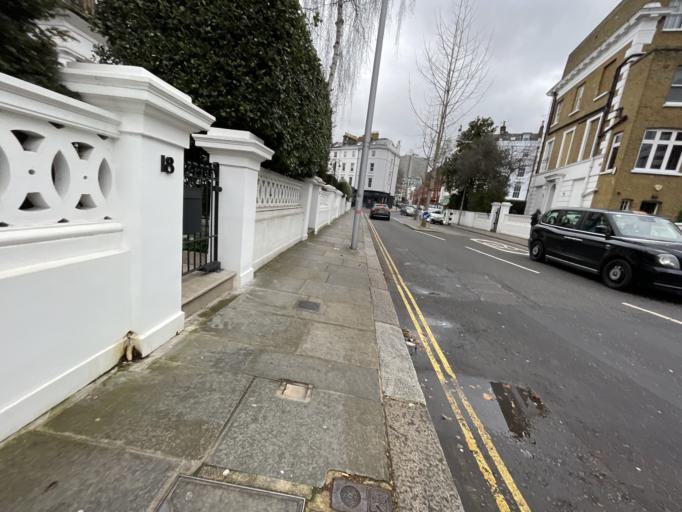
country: GB
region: England
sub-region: Greater London
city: Chelsea
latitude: 51.4903
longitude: -0.1828
